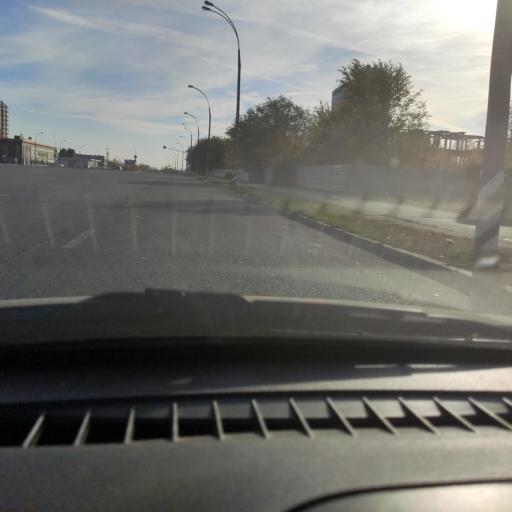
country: RU
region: Samara
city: Tol'yatti
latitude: 53.5043
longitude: 49.2752
